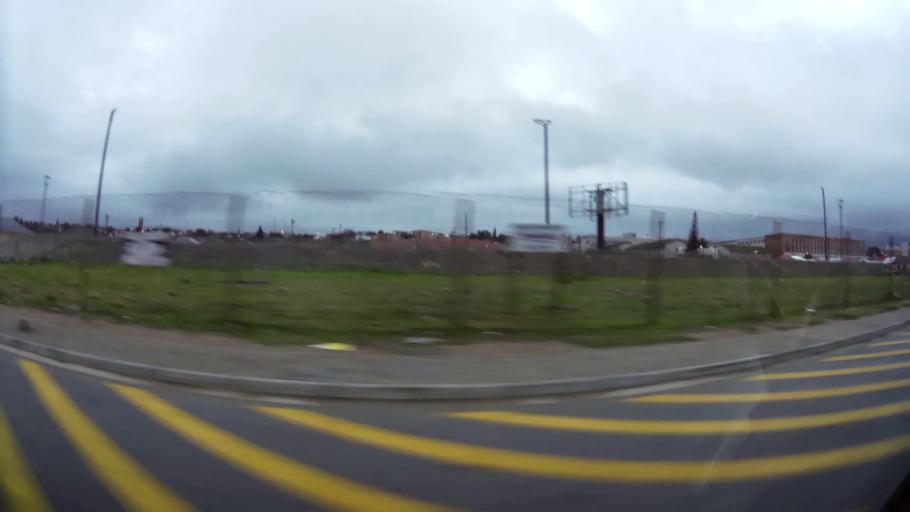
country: ZA
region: Eastern Cape
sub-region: Nelson Mandela Bay Metropolitan Municipality
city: Port Elizabeth
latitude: -33.9379
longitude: 25.5906
